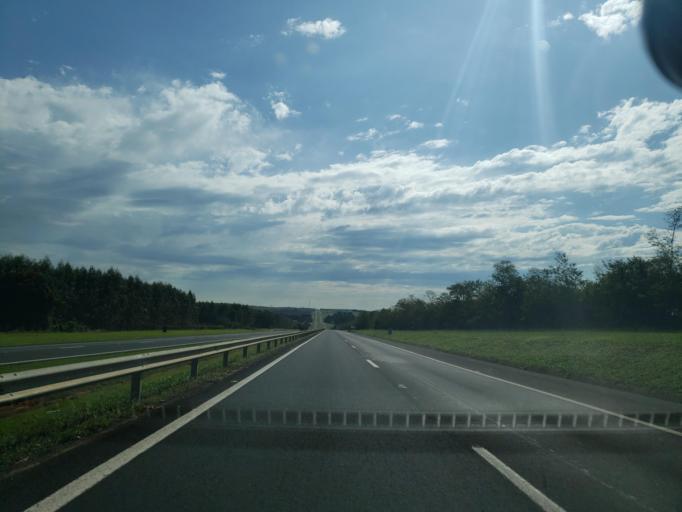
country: BR
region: Sao Paulo
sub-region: Pirajui
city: Pirajui
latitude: -21.9018
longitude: -49.5283
